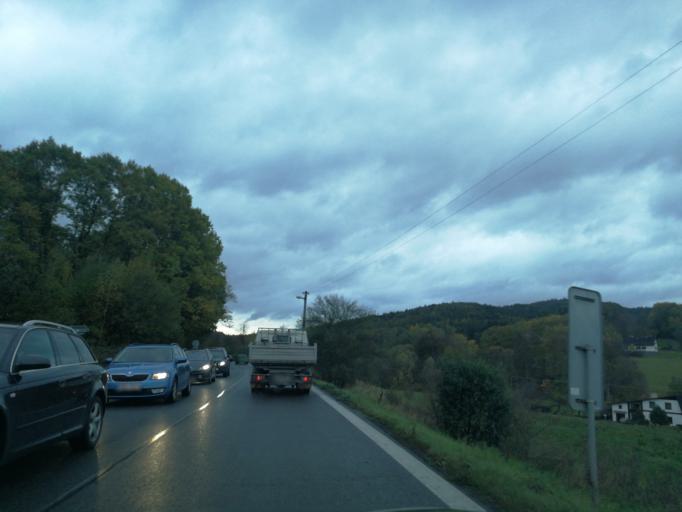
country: CZ
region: Zlin
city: Valasske Mezirici
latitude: 49.4977
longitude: 17.9918
